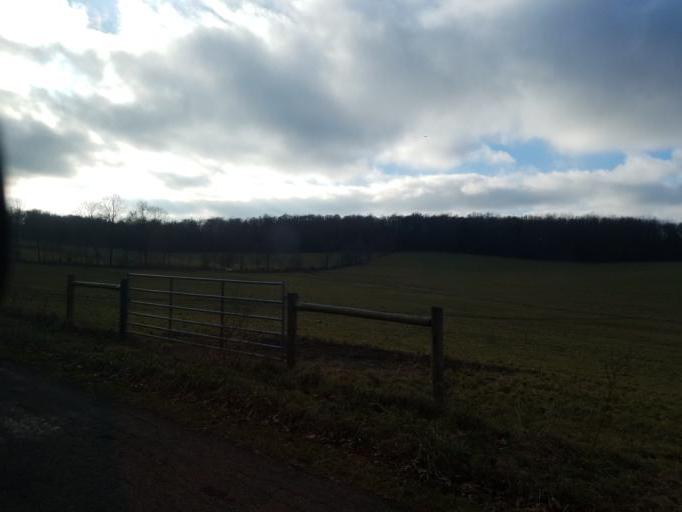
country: US
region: Ohio
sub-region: Sandusky County
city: Bellville
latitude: 40.5882
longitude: -82.3717
